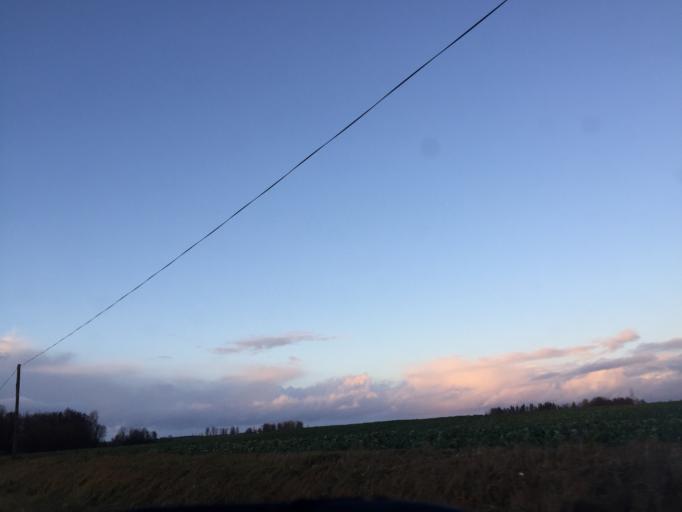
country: LV
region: Burtnieki
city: Matisi
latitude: 57.7094
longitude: 25.1531
